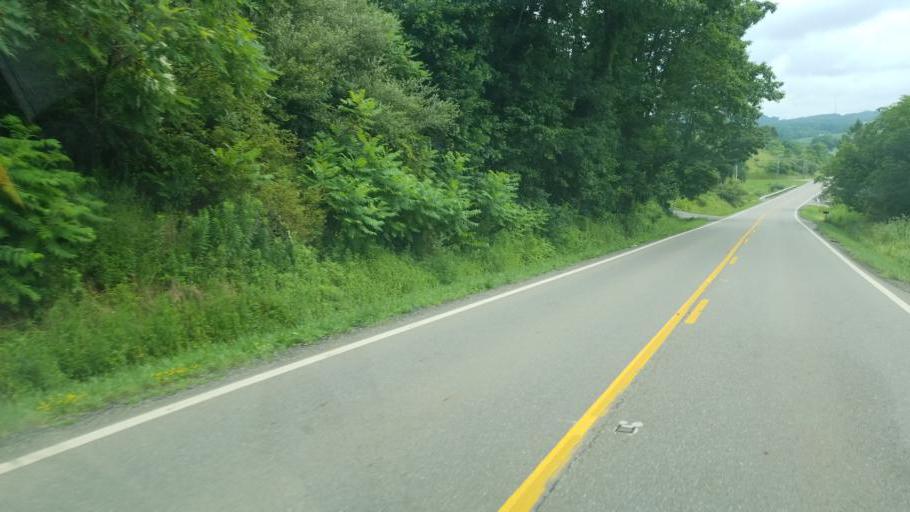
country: US
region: Ohio
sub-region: Columbiana County
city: Lisbon
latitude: 40.7166
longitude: -80.7941
